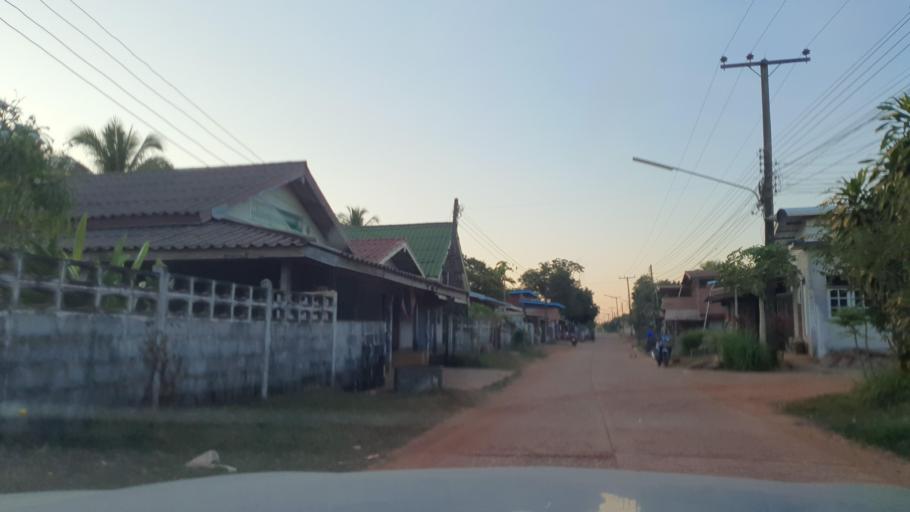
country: TH
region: Nakhon Phanom
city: Ban Phaeng
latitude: 17.8283
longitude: 104.2665
